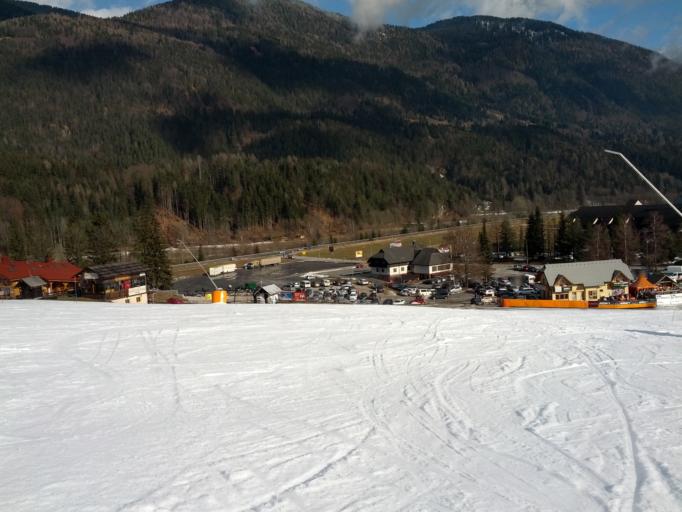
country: SI
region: Kranjska Gora
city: Kranjska Gora
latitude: 46.4851
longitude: 13.7761
